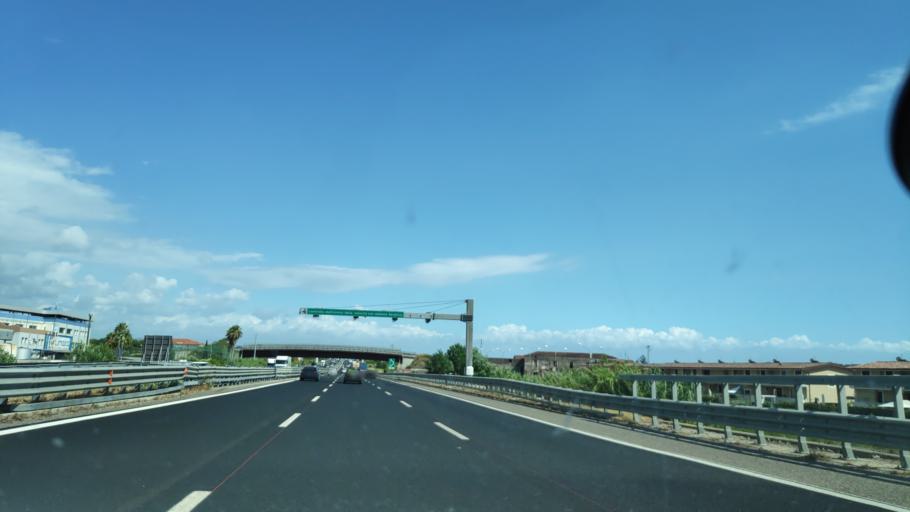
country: IT
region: Campania
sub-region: Provincia di Salerno
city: Pontecagnano
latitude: 40.6526
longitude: 14.8734
